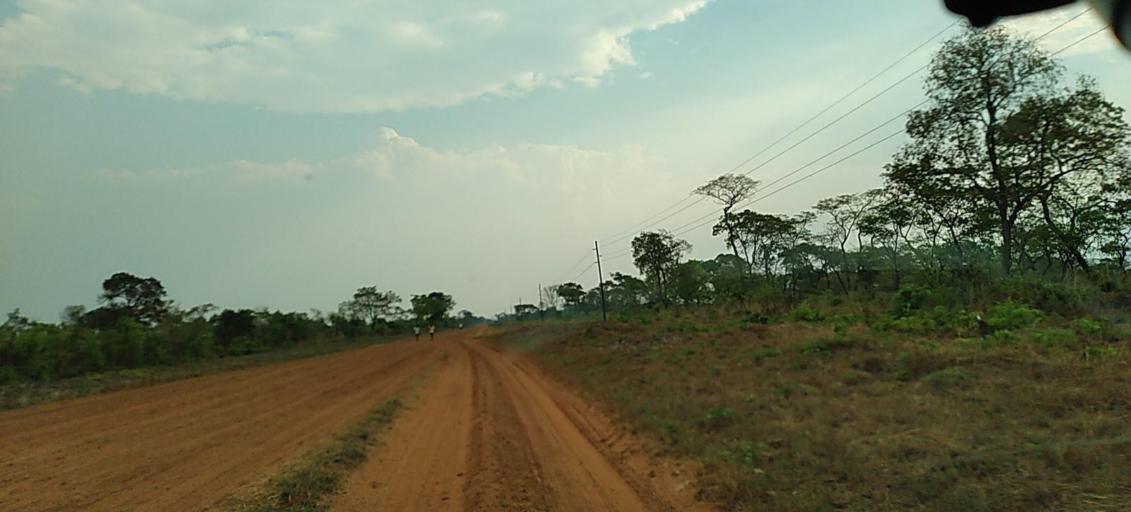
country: ZM
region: North-Western
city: Kabompo
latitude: -13.8890
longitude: 23.6605
